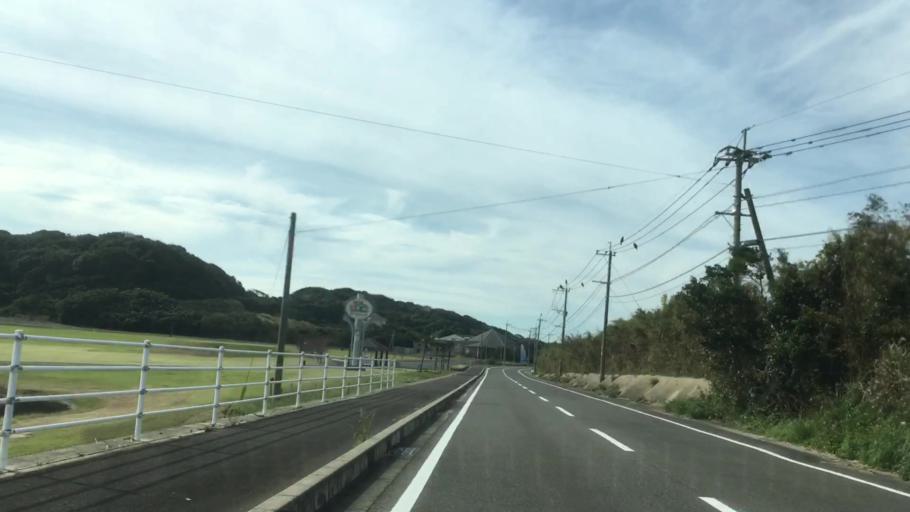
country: JP
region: Nagasaki
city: Sasebo
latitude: 33.0175
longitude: 129.5741
